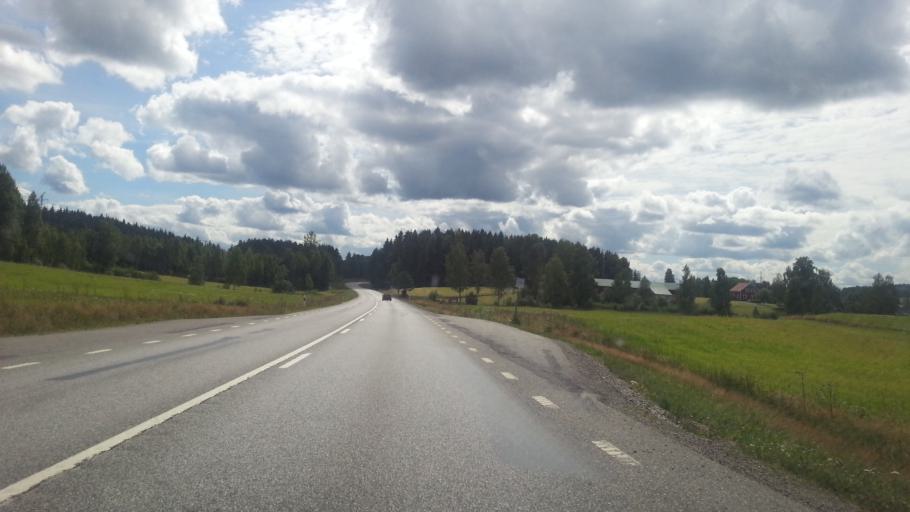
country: SE
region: OErebro
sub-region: Lindesbergs Kommun
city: Stora
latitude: 59.8083
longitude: 15.1450
